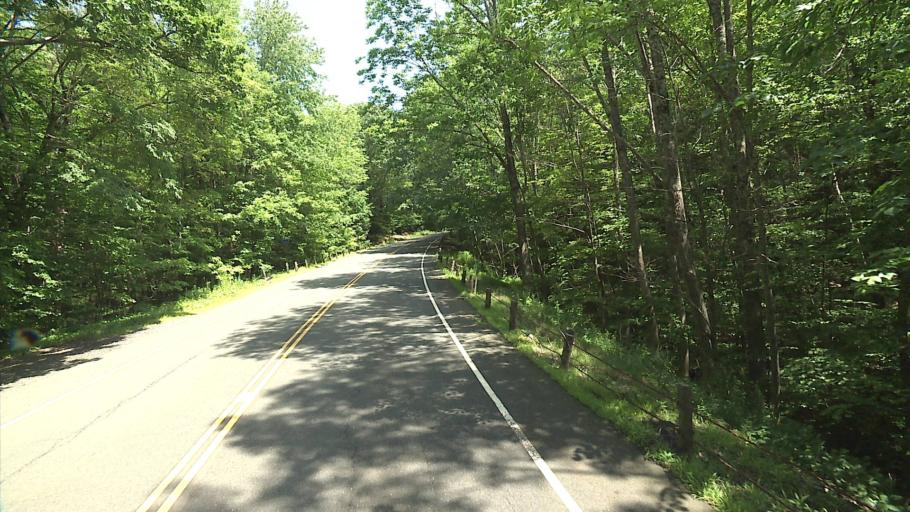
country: US
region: Massachusetts
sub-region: Hampden County
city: Granville
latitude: 42.0161
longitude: -72.9198
